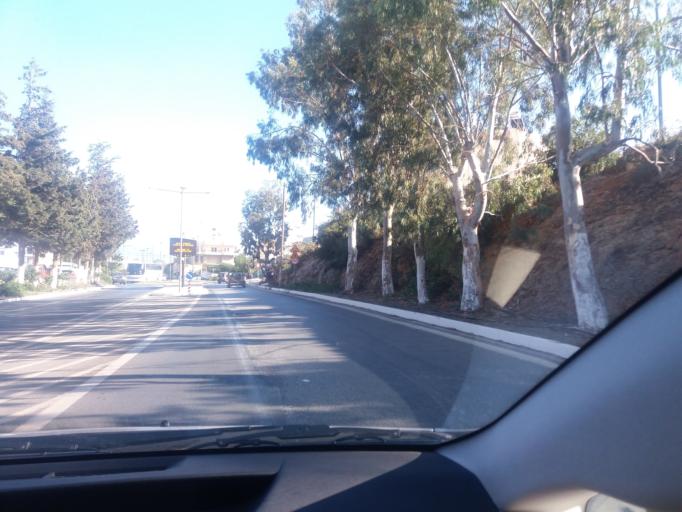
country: GR
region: Crete
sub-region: Nomos Lasithiou
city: Agios Nikolaos
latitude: 35.1985
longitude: 25.7082
